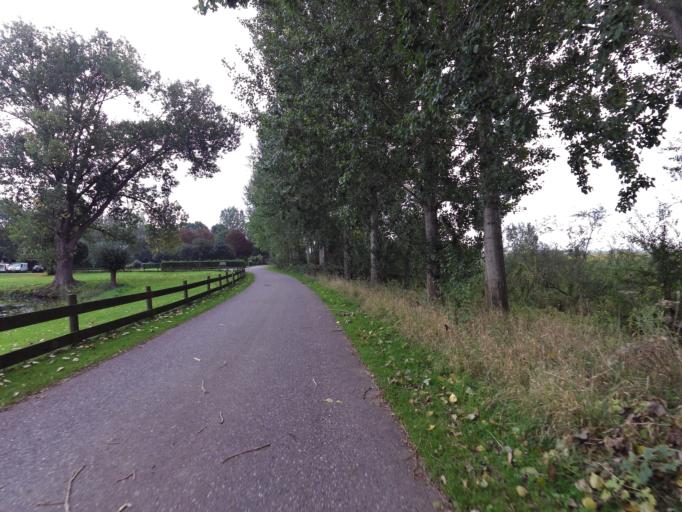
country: NL
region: Gelderland
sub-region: Gemeente Zevenaar
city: Zevenaar
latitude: 51.9082
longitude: 6.0986
